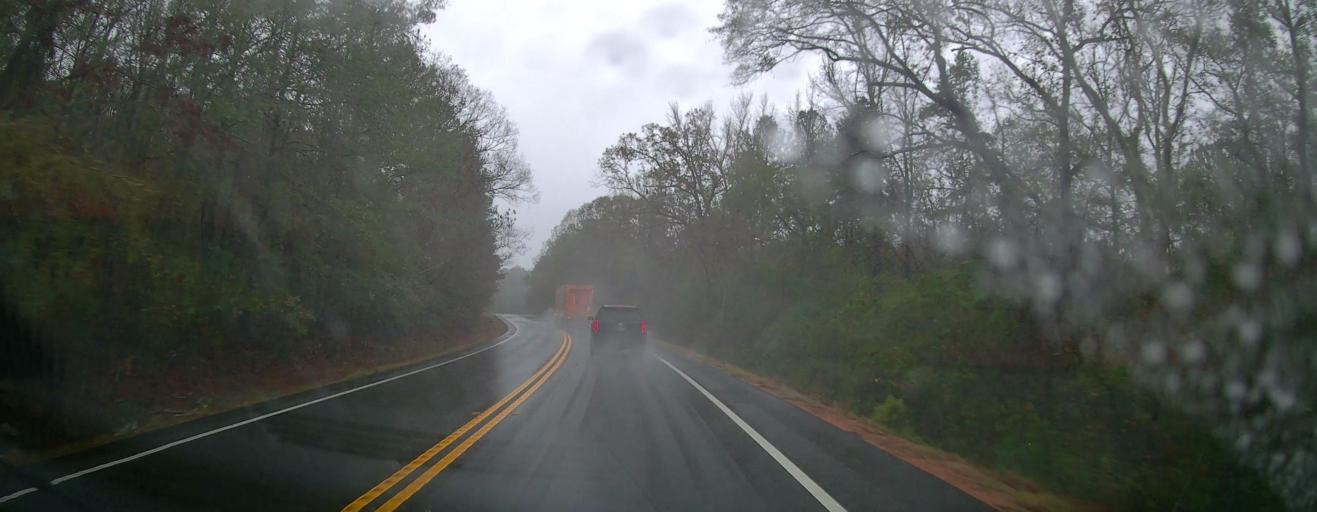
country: US
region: Georgia
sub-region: Putnam County
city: Eatonton
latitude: 33.2209
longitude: -83.4295
